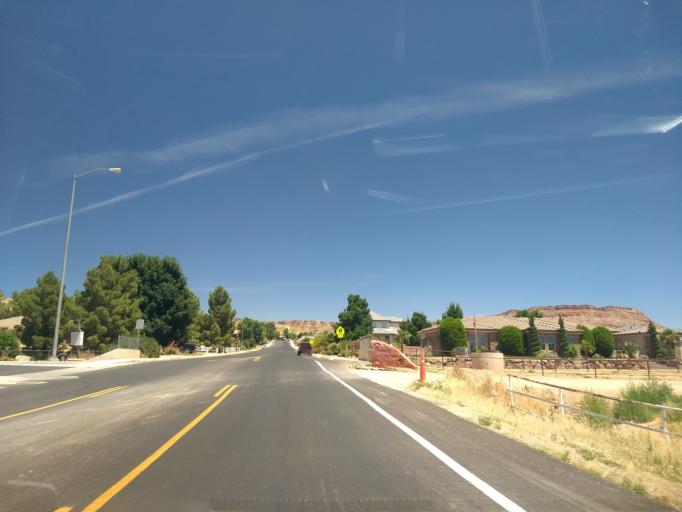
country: US
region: Utah
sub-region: Washington County
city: Washington
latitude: 37.0889
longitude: -113.4971
